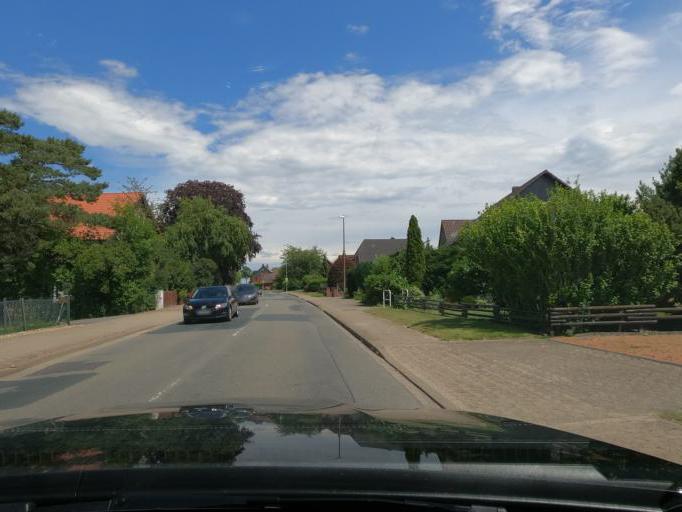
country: DE
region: Lower Saxony
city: Sohlde
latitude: 52.1858
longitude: 10.2027
